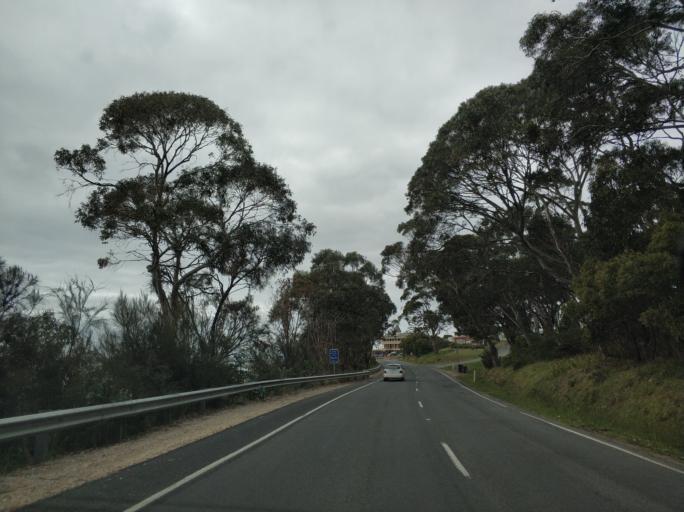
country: AU
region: Victoria
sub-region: Surf Coast
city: Anglesea
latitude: -38.5459
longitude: 143.9825
